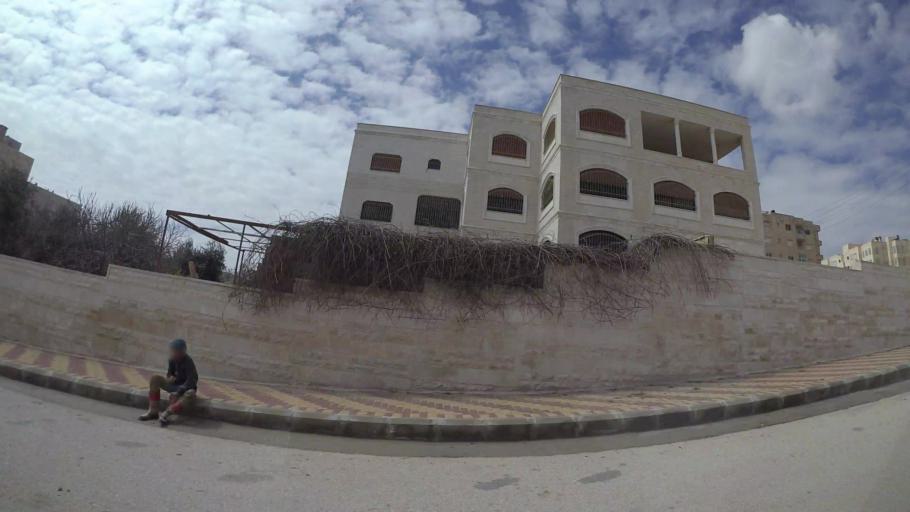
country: JO
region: Amman
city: Al Jubayhah
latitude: 31.9972
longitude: 35.9103
